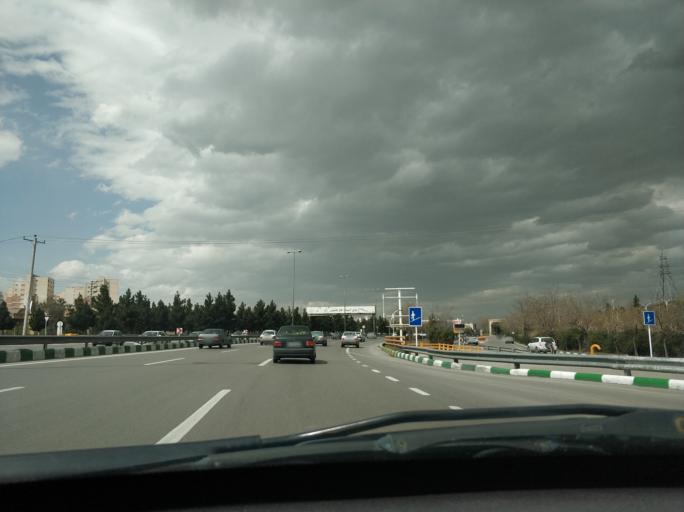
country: IR
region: Razavi Khorasan
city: Mashhad
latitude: 36.2745
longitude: 59.5555
